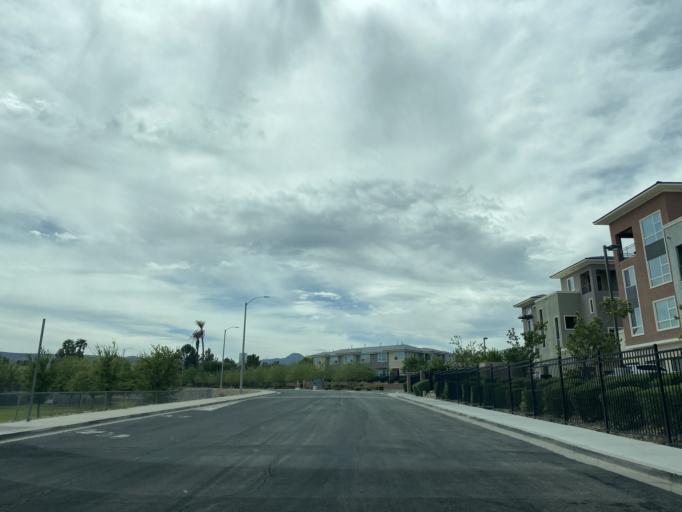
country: US
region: Nevada
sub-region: Clark County
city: Whitney
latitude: 36.0233
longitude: -115.0795
